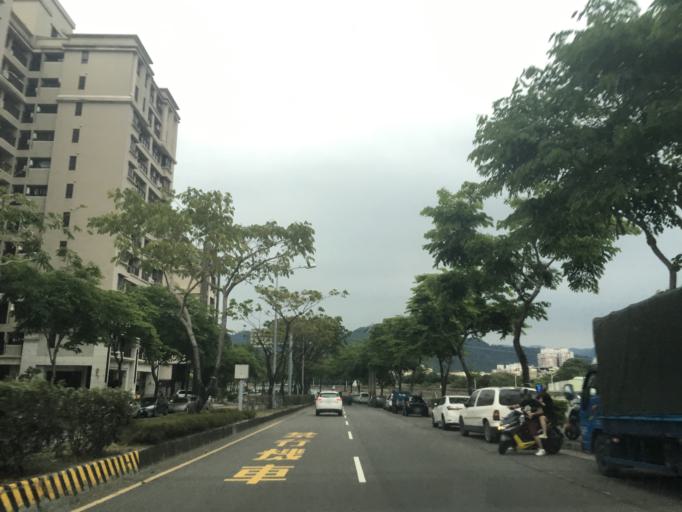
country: TW
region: Taiwan
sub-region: Taichung City
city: Taichung
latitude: 24.1359
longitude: 120.7154
